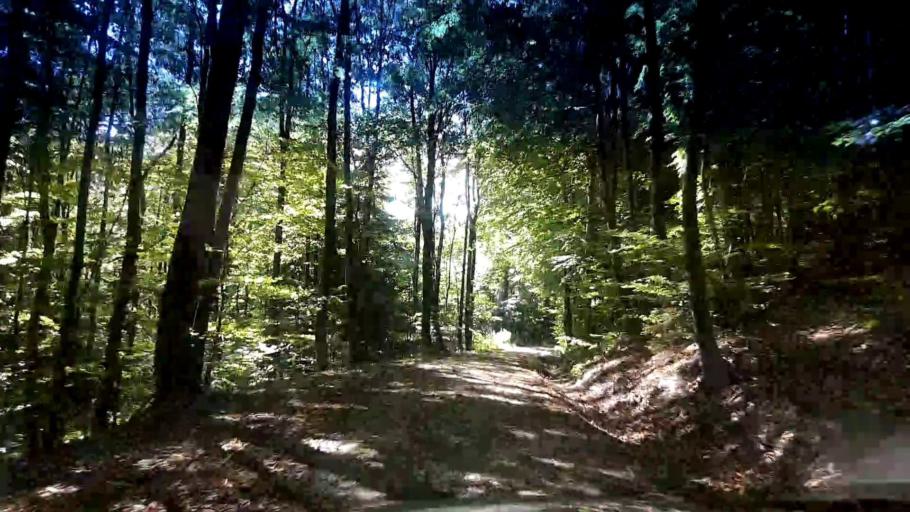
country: DE
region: Bavaria
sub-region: Upper Franconia
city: Litzendorf
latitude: 49.8846
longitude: 11.0333
